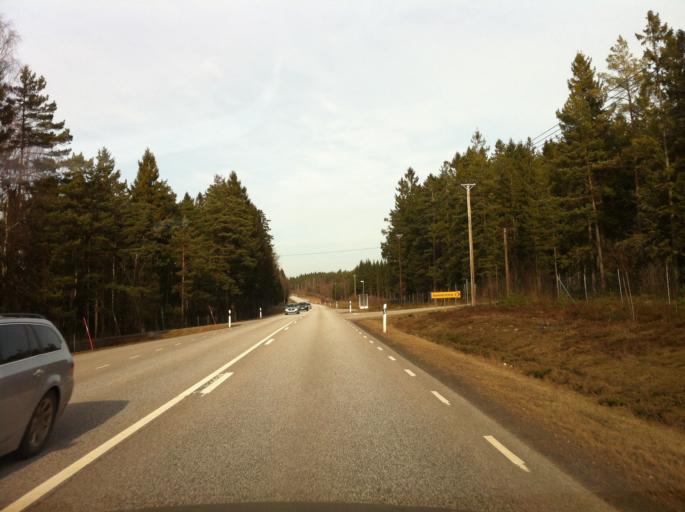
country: SE
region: Vaestra Goetaland
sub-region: Gullspangs Kommun
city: Gullspang
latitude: 58.9436
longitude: 14.0462
